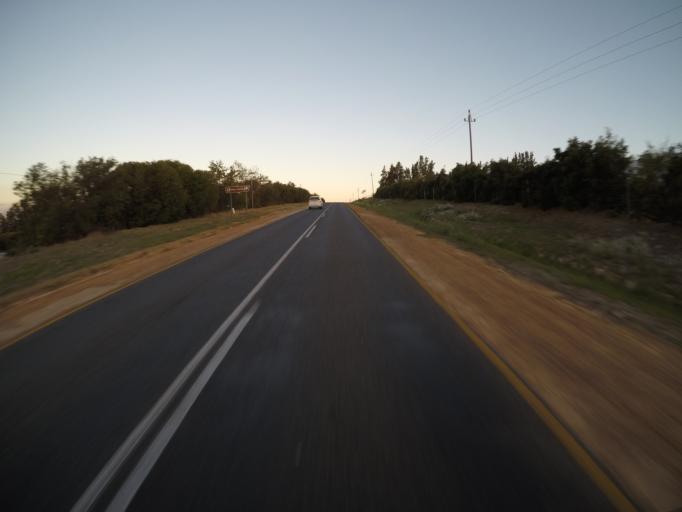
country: ZA
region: Western Cape
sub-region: Cape Winelands District Municipality
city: Paarl
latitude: -33.8087
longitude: 18.9034
